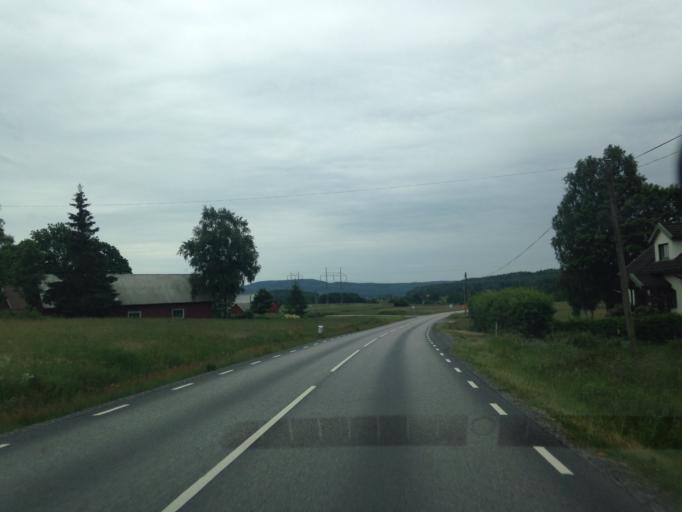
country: SE
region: Vaestra Goetaland
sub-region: Marks Kommun
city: Horred
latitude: 57.4788
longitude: 12.5168
